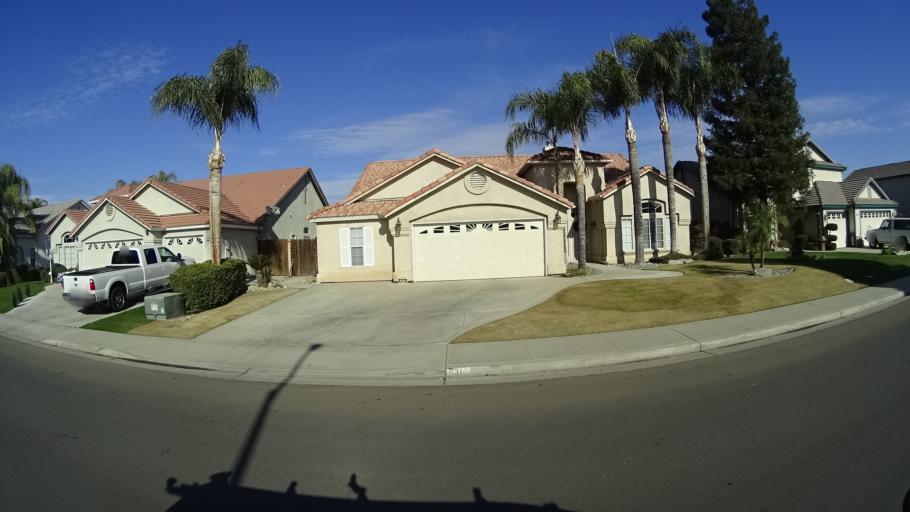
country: US
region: California
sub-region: Kern County
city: Greenacres
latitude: 35.4063
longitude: -119.0953
